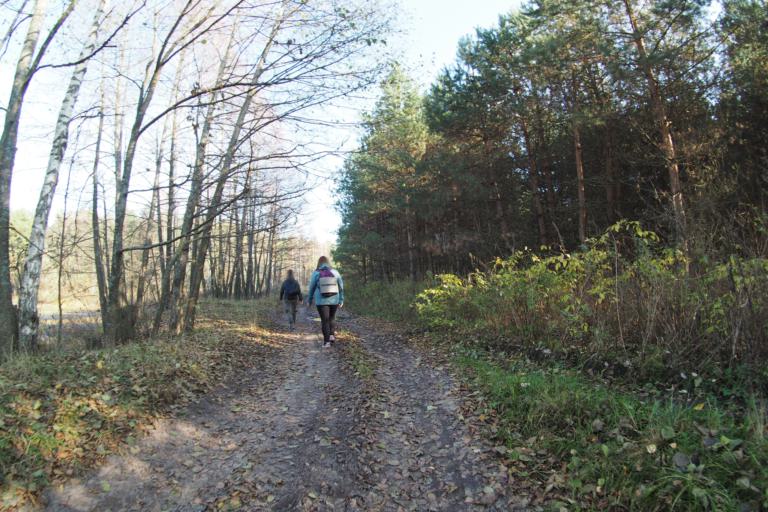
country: RU
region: Moskovskaya
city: Davydovo
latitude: 55.5453
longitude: 38.8195
